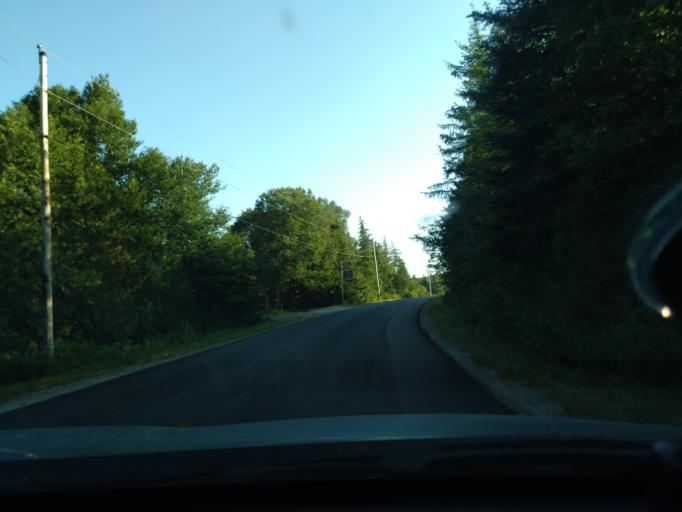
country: US
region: Maine
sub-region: Washington County
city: East Machias
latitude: 44.6991
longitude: -67.1579
